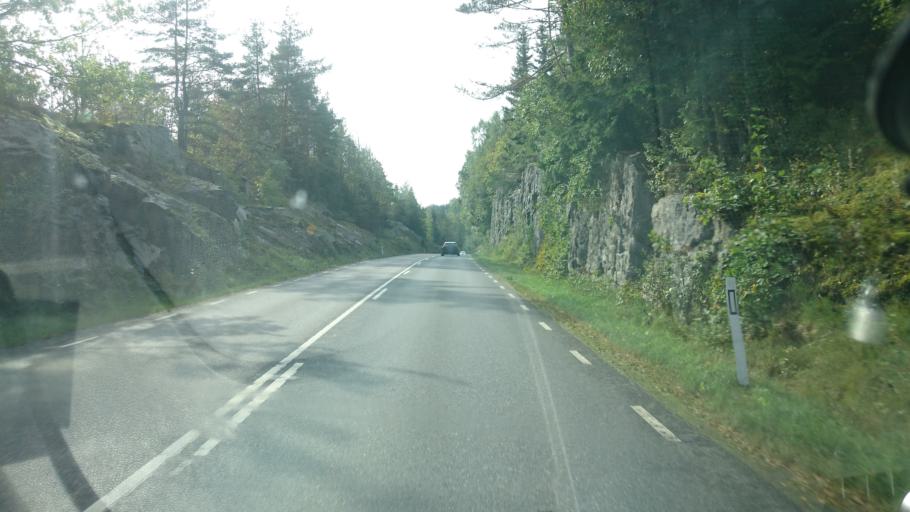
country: SE
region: Vaestra Goetaland
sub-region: Alingsas Kommun
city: Sollebrunn
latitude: 58.0352
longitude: 12.4654
